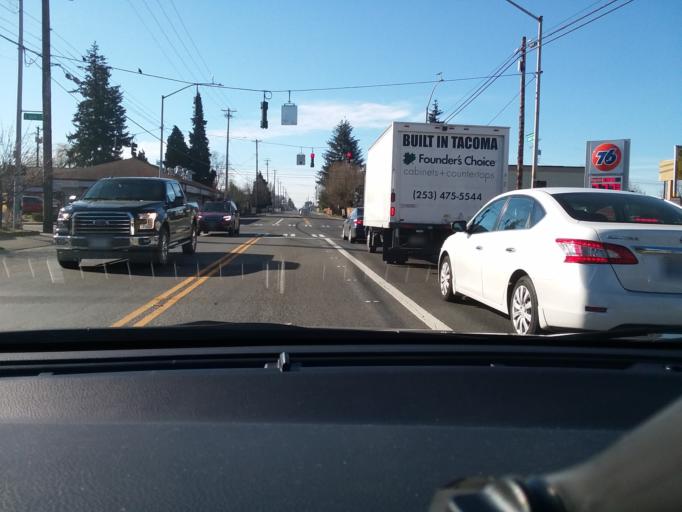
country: US
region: Washington
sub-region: Pierce County
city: Midland
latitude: 47.2067
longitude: -122.4209
